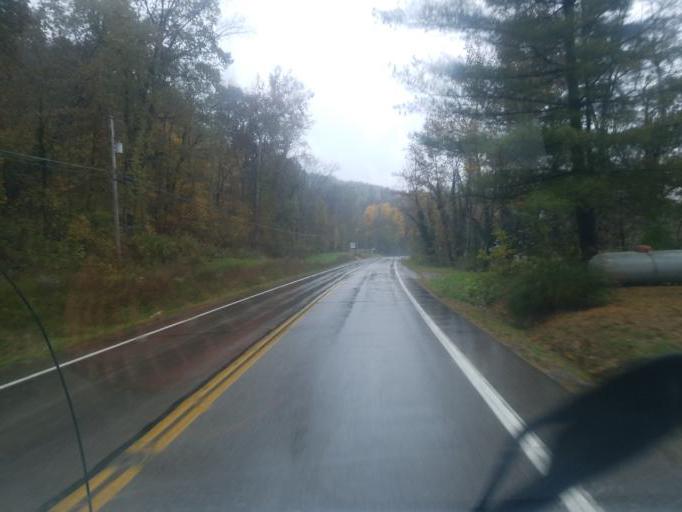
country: US
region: Ohio
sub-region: Morgan County
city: McConnelsville
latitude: 39.7592
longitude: -81.8940
